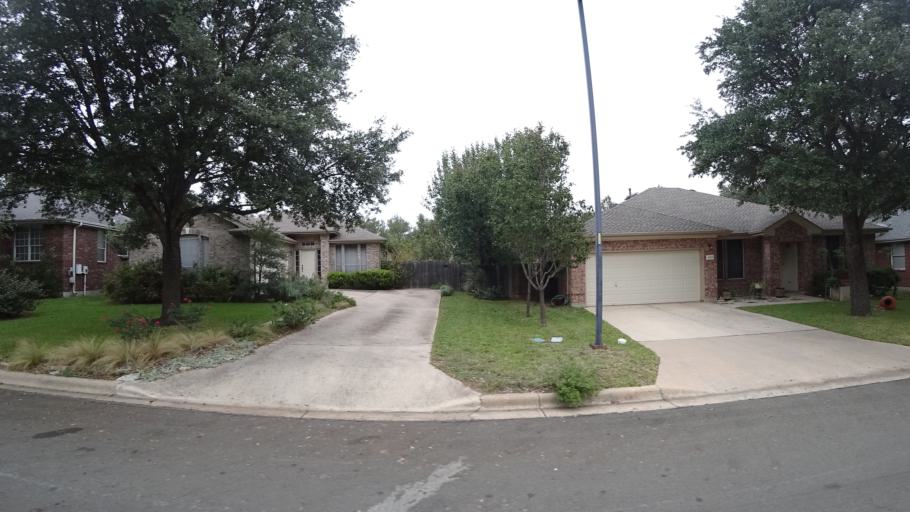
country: US
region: Texas
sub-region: Travis County
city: Shady Hollow
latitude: 30.2118
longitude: -97.8884
